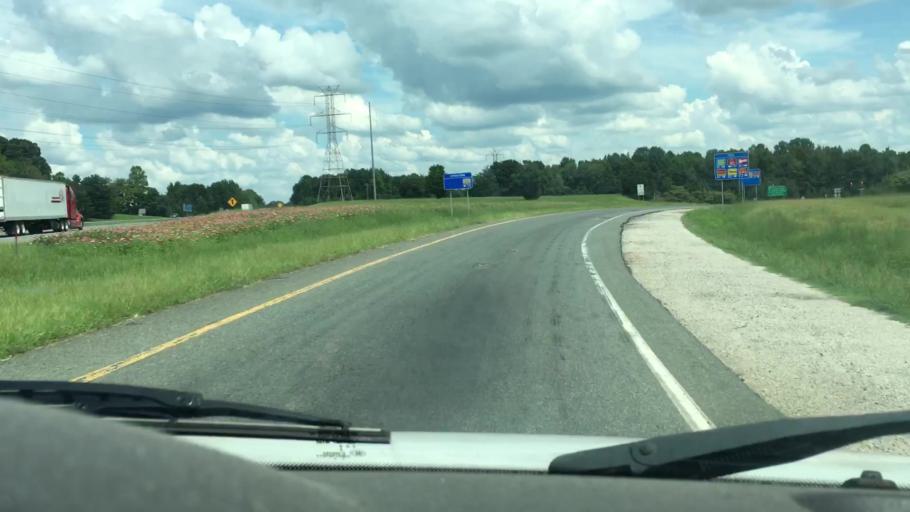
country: US
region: North Carolina
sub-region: Iredell County
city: Troutman
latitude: 35.6710
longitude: -80.8579
